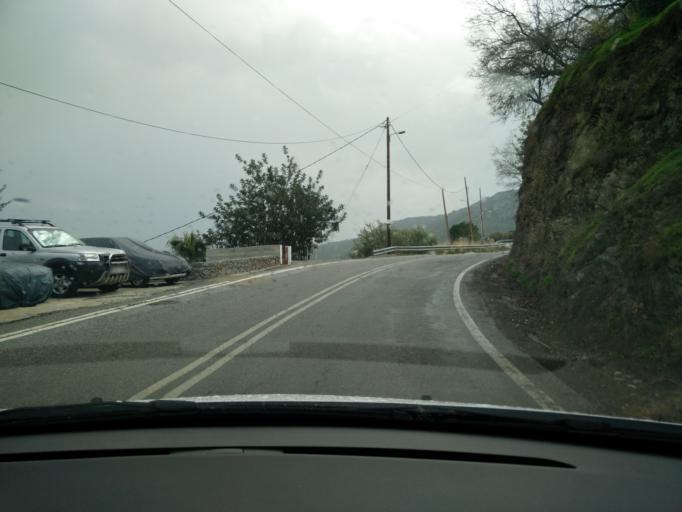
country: GR
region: Crete
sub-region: Nomos Lasithiou
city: Kritsa
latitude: 35.1547
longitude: 25.6443
